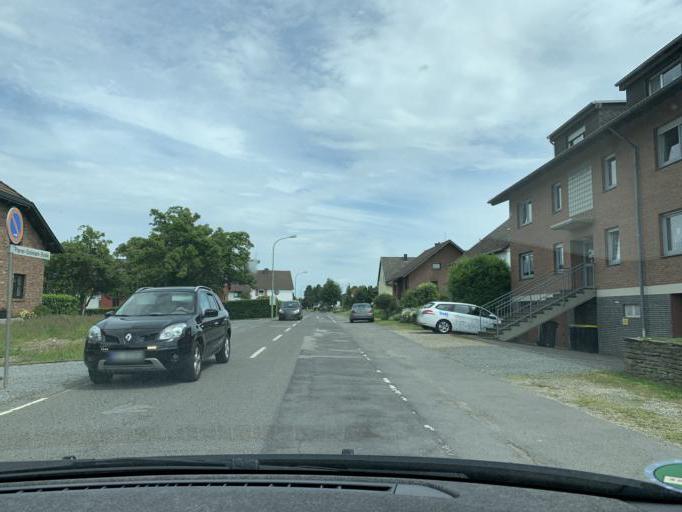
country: DE
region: North Rhine-Westphalia
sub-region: Regierungsbezirk Koln
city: Hurtgenwald
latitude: 50.6871
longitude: 6.3681
